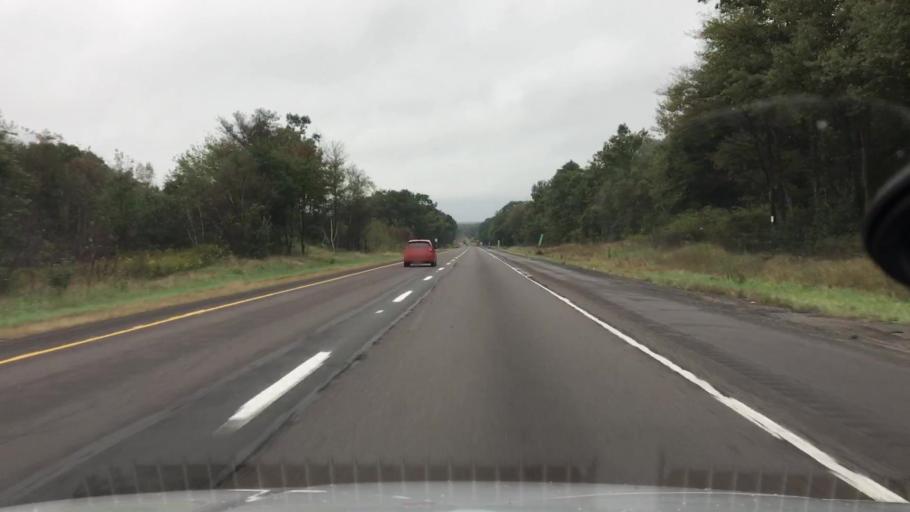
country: US
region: Pennsylvania
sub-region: Carbon County
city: Towamensing Trails
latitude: 41.0823
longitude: -75.6407
